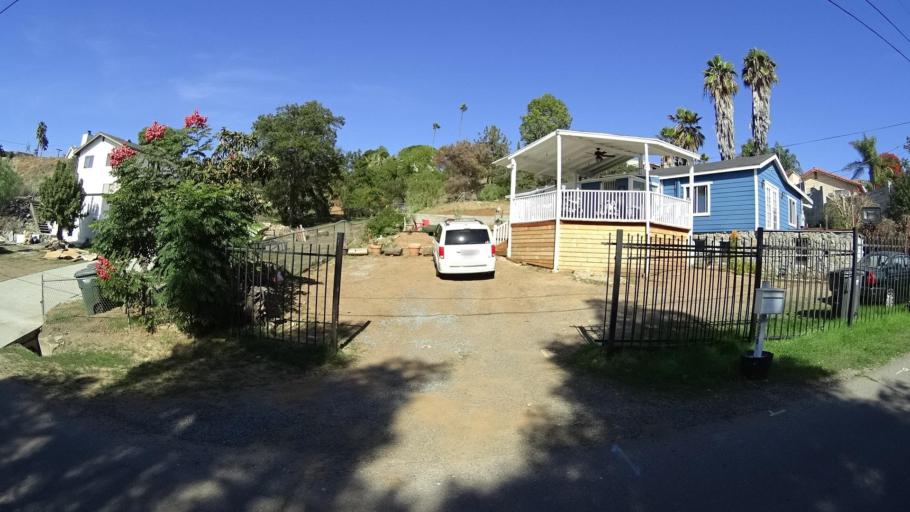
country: US
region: California
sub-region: San Diego County
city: Casa de Oro-Mount Helix
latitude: 32.7510
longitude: -116.9782
